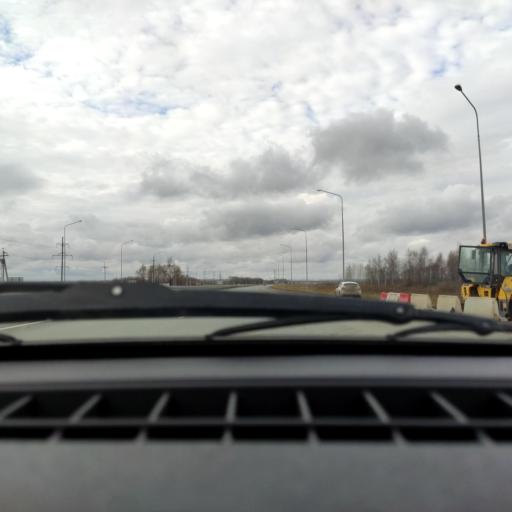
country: RU
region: Bashkortostan
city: Asanovo
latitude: 54.9051
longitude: 55.6174
